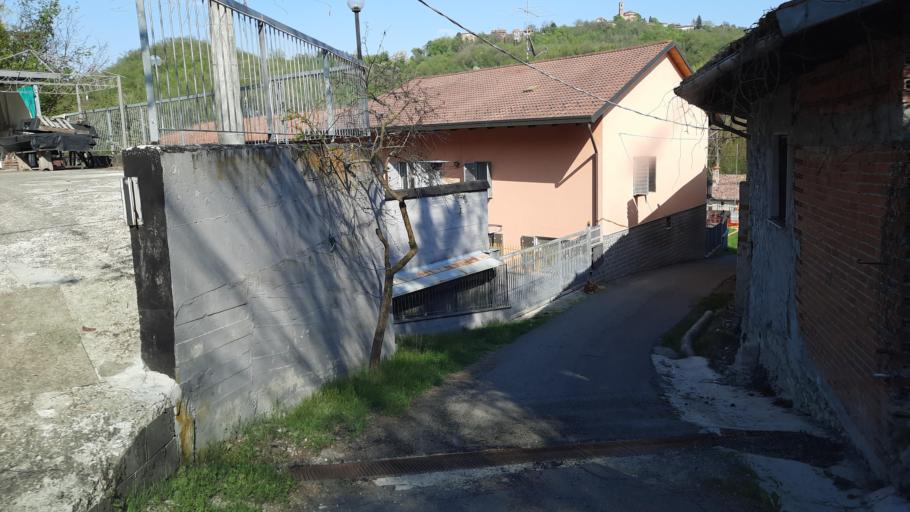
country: IT
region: Piedmont
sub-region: Provincia di Alessandria
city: Villamiroglio
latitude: 45.1339
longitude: 8.1777
